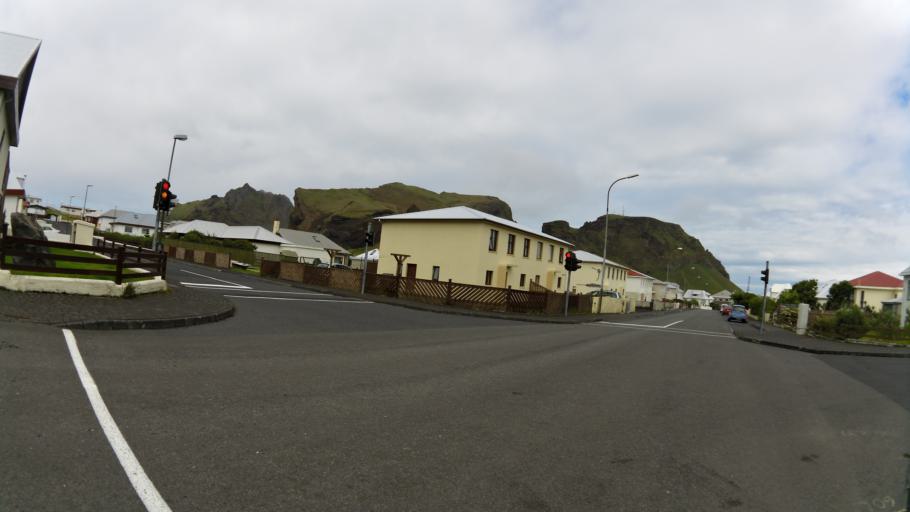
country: IS
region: South
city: Vestmannaeyjar
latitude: 63.4380
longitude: -20.2770
